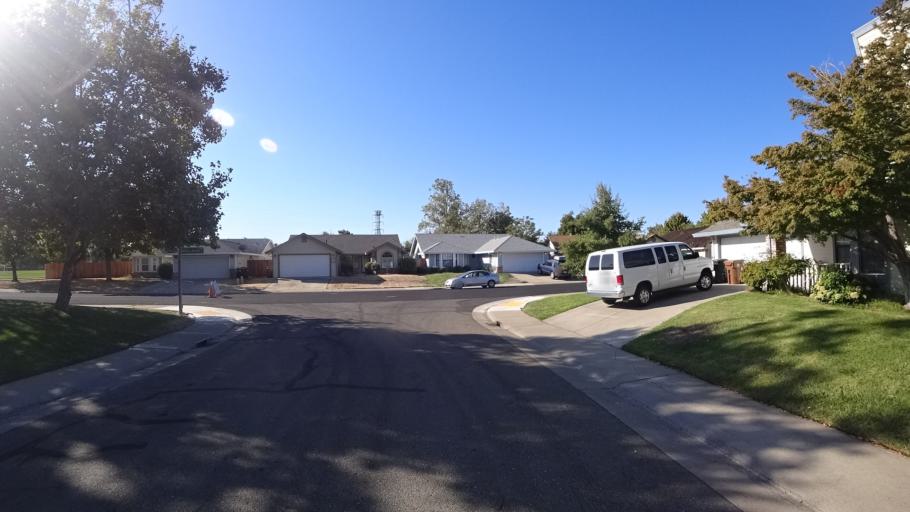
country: US
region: California
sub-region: Sacramento County
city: Laguna
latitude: 38.4283
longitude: -121.4431
